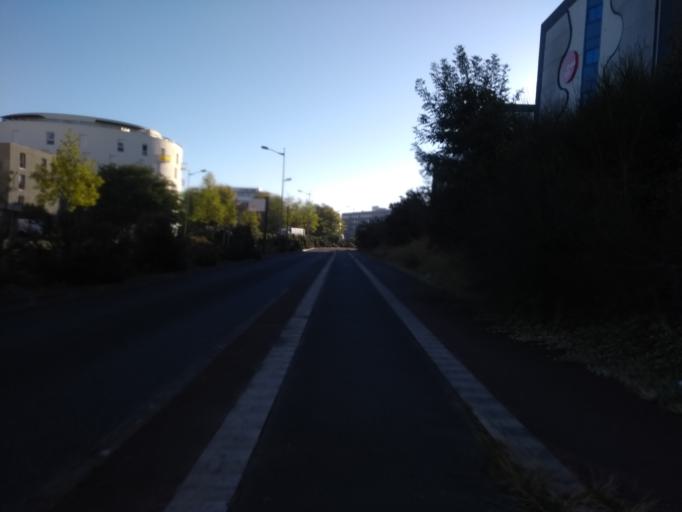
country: FR
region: Aquitaine
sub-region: Departement de la Gironde
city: Talence
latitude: 44.8078
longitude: -0.6028
